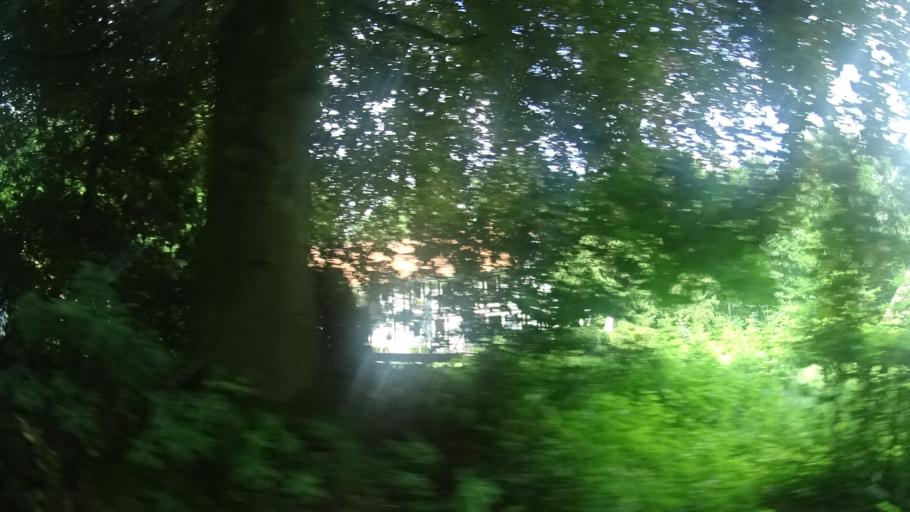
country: DE
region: Lower Saxony
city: Bad Munder am Deister
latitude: 52.1838
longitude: 9.4259
